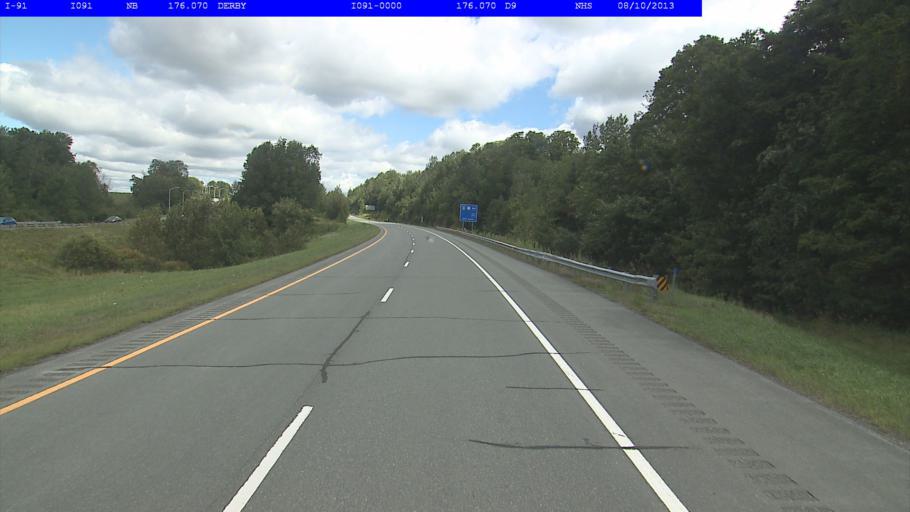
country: US
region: Vermont
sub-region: Orleans County
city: Newport
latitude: 44.9907
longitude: -72.1027
